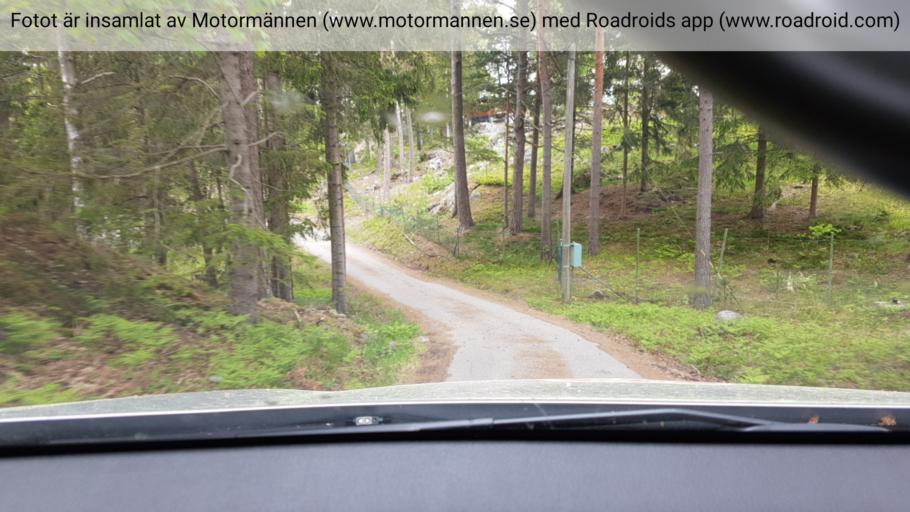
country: SE
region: Stockholm
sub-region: Haninge Kommun
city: Jordbro
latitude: 59.0229
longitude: 18.0998
